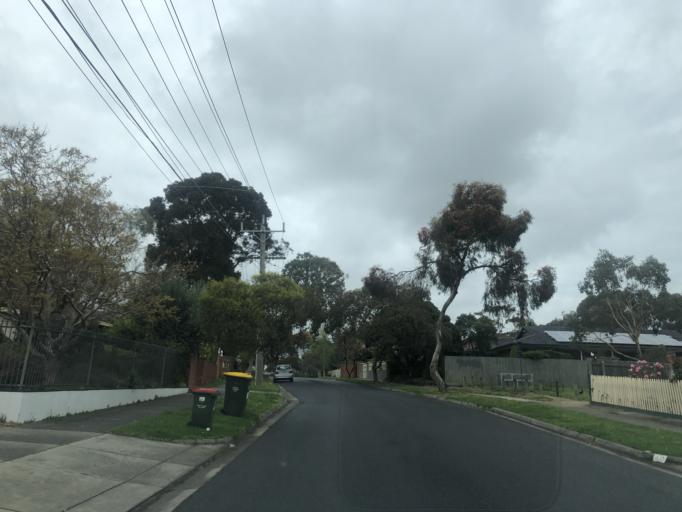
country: AU
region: Victoria
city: Burwood East
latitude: -37.8553
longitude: 145.1366
